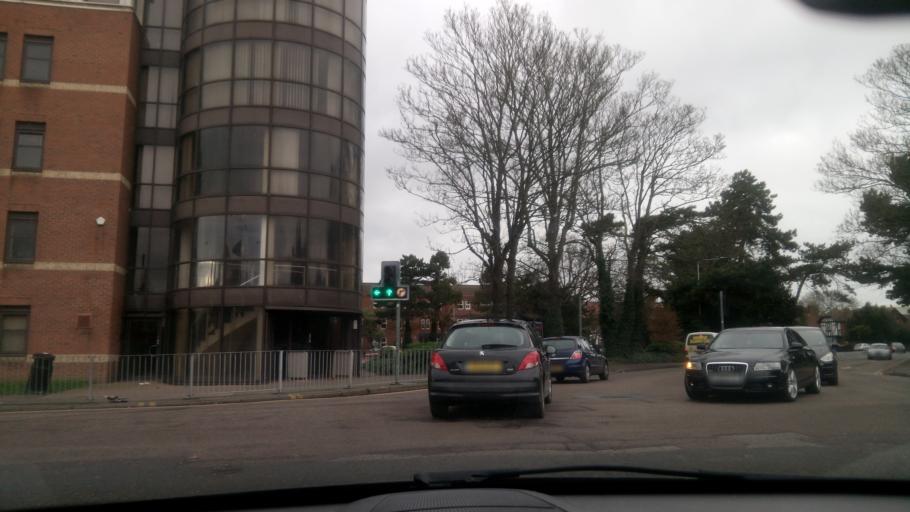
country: GB
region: England
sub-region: Peterborough
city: Peterborough
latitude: 52.5788
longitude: -0.2388
